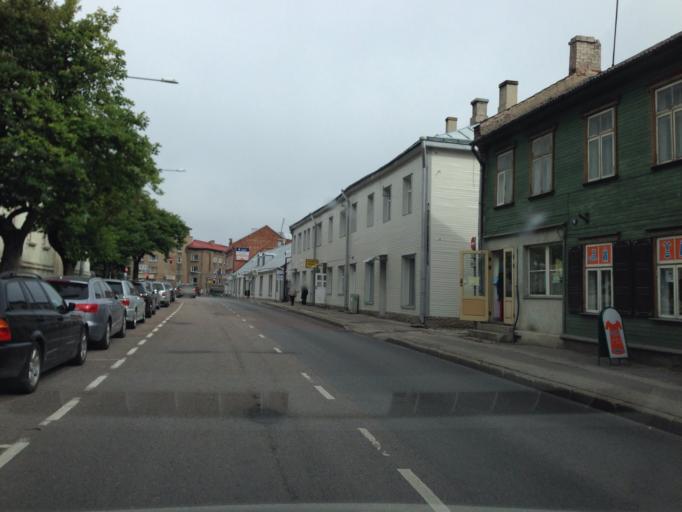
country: EE
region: Tartu
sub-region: Tartu linn
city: Tartu
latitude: 58.3729
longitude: 26.7228
